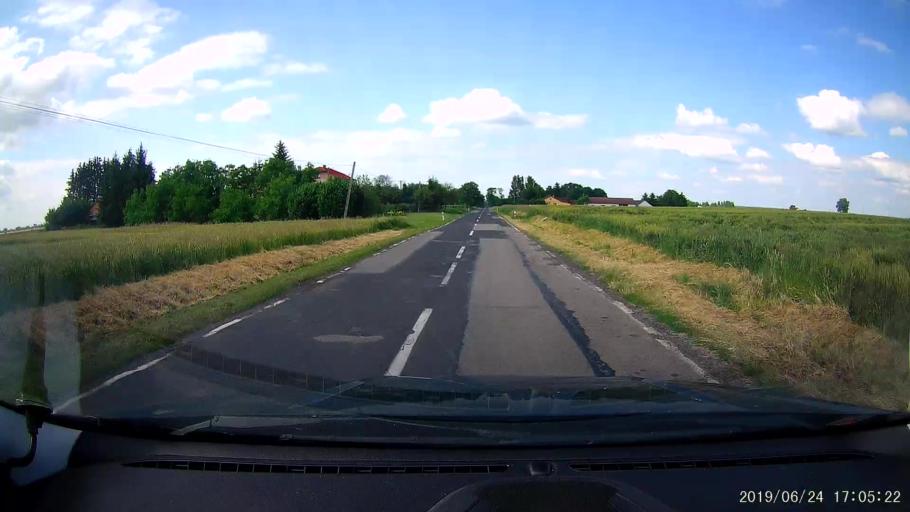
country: PL
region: Lublin Voivodeship
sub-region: Powiat hrubieszowski
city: Dolhobyczow
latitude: 50.5743
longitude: 23.9641
